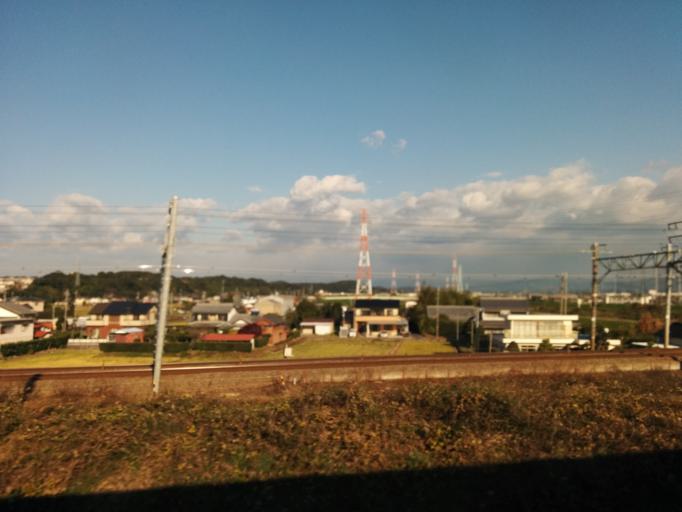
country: JP
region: Shizuoka
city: Fukuroi
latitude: 34.7244
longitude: 137.8943
